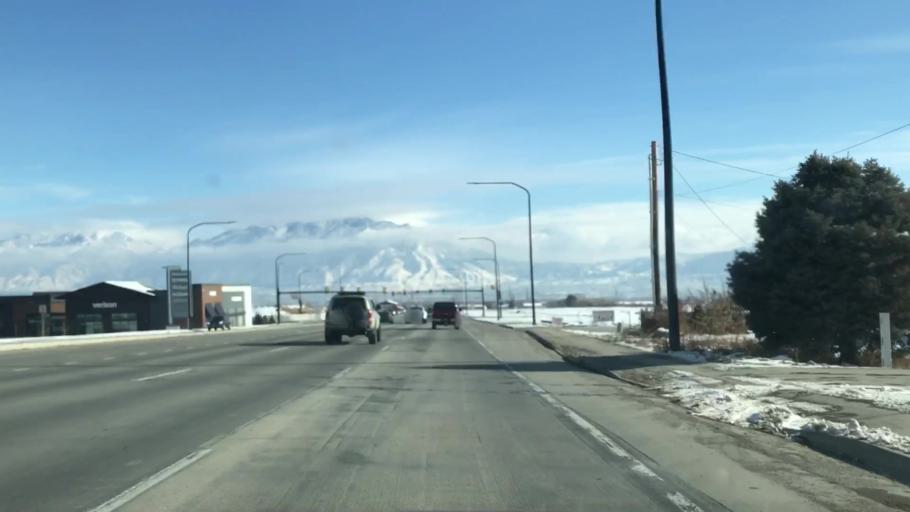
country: US
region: Utah
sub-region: Salt Lake County
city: Herriman
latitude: 40.5078
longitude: -112.0009
